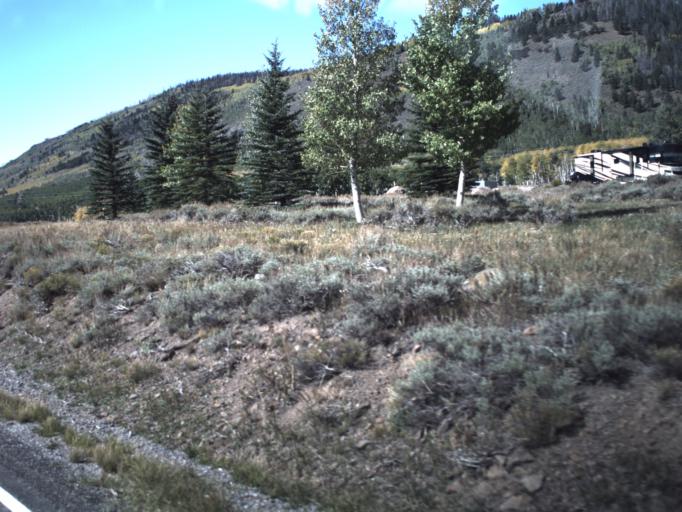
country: US
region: Utah
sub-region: Wayne County
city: Loa
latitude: 38.5322
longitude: -111.7394
